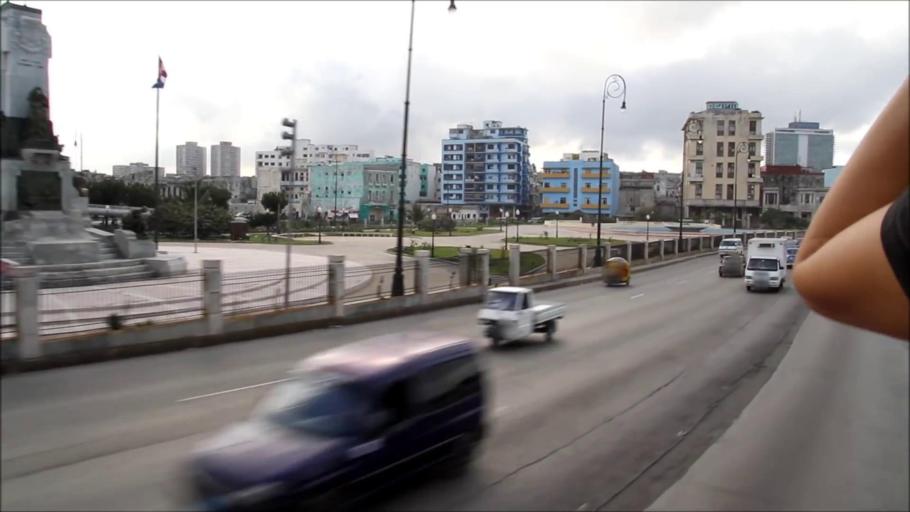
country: CU
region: La Habana
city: Centro Habana
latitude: 23.1417
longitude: -82.3721
